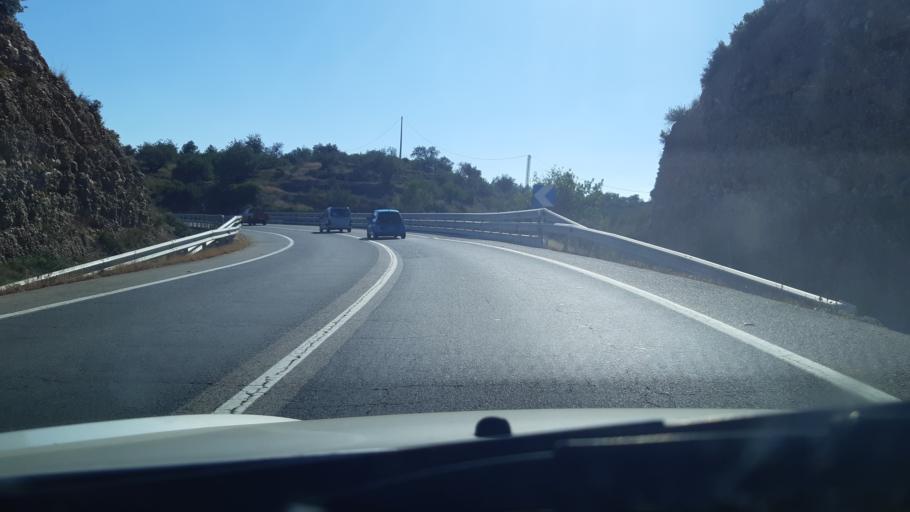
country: ES
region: Catalonia
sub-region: Provincia de Tarragona
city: Tivenys
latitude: 40.8797
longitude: 0.4974
